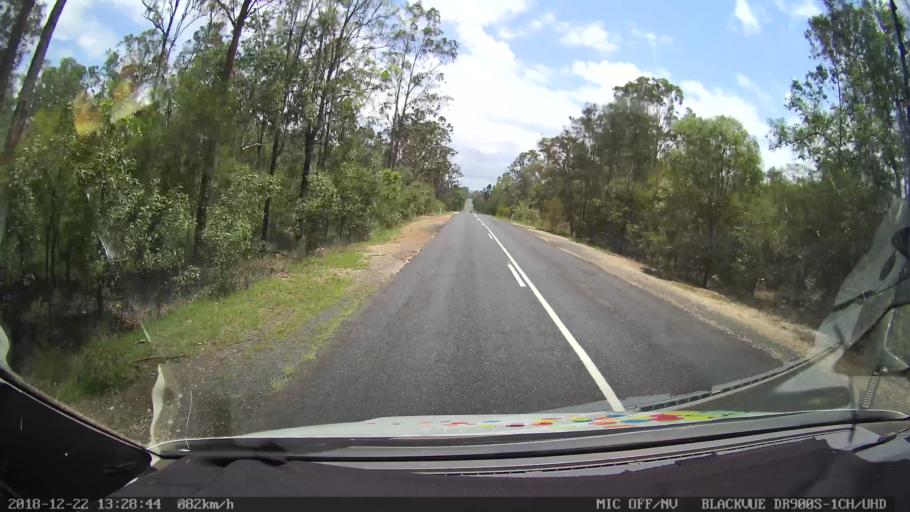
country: AU
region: New South Wales
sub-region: Clarence Valley
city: Coutts Crossing
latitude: -29.8365
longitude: 152.8852
